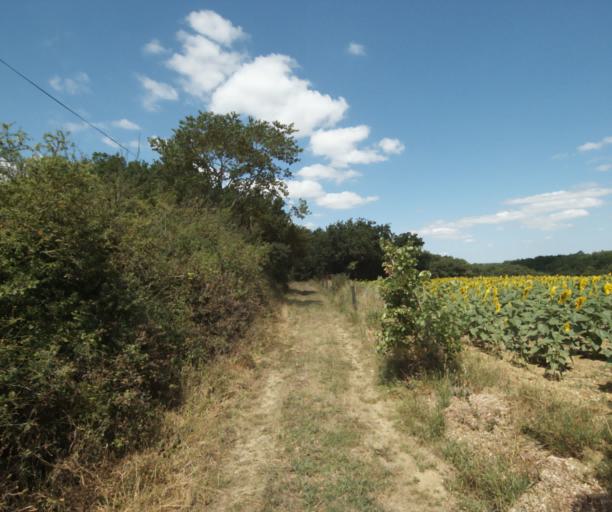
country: FR
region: Midi-Pyrenees
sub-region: Departement de la Haute-Garonne
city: Saint-Felix-Lauragais
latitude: 43.4708
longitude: 1.8569
